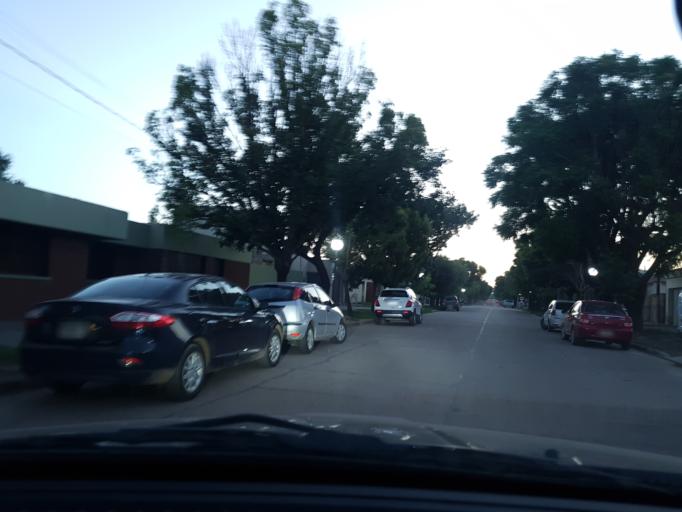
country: AR
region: Cordoba
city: Las Perdices
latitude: -32.7601
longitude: -63.7850
